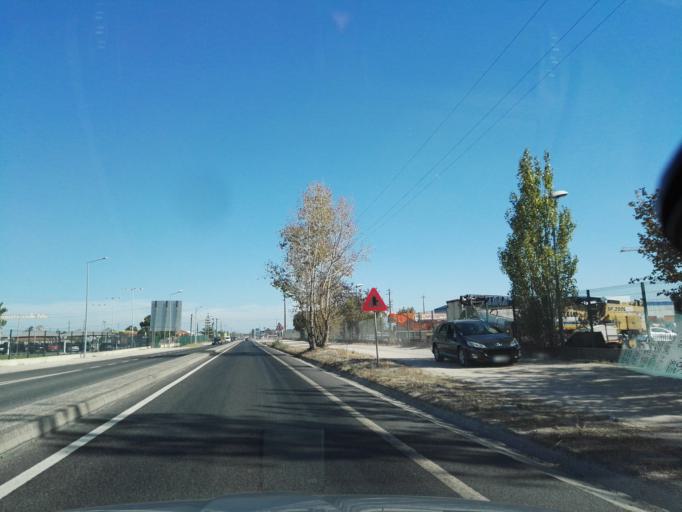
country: PT
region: Santarem
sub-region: Benavente
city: Samora Correia
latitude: 38.9190
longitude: -8.8738
